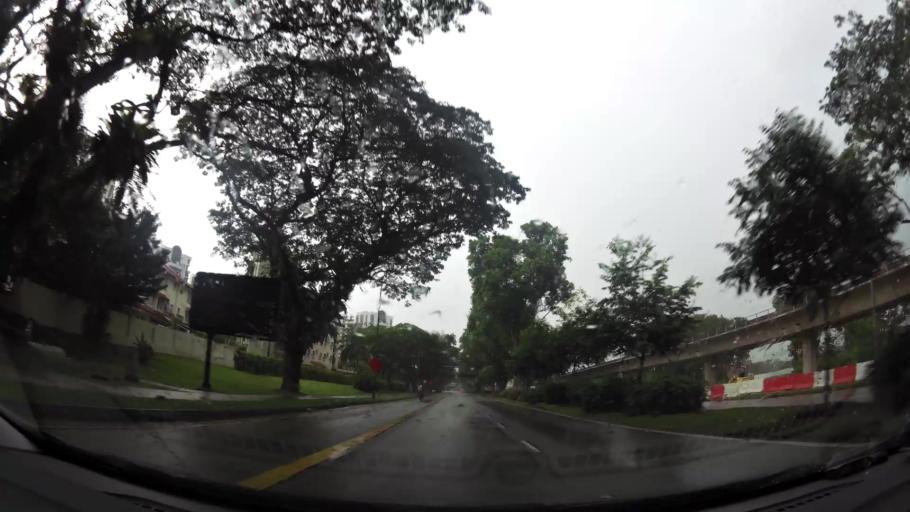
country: MY
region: Johor
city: Kampung Pasir Gudang Baru
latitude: 1.3915
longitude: 103.8382
